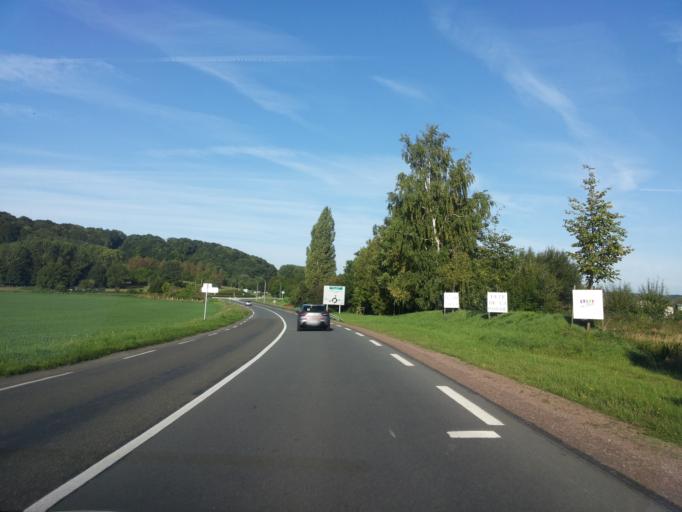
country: FR
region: Picardie
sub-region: Departement de l'Aisne
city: Crepy
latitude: 49.5970
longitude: 3.5266
